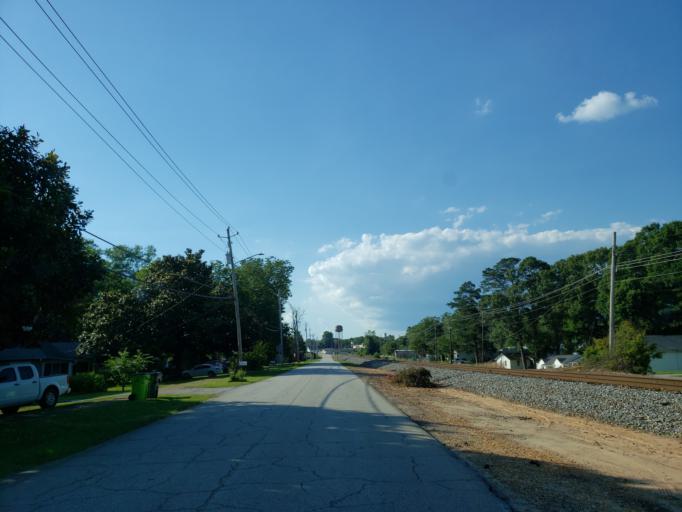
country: US
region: Georgia
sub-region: Haralson County
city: Bremen
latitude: 33.7143
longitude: -85.1456
